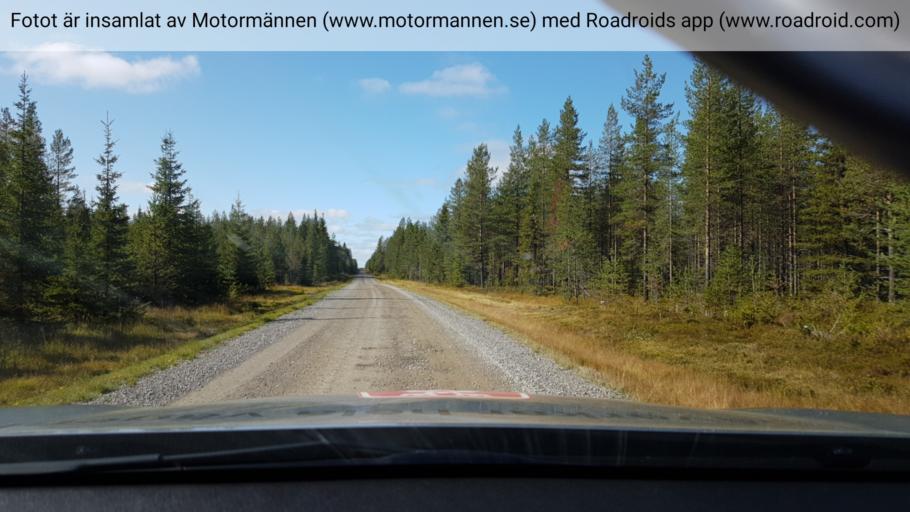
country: SE
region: Vaesterbotten
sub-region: Mala Kommun
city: Mala
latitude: 65.2130
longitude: 19.1051
